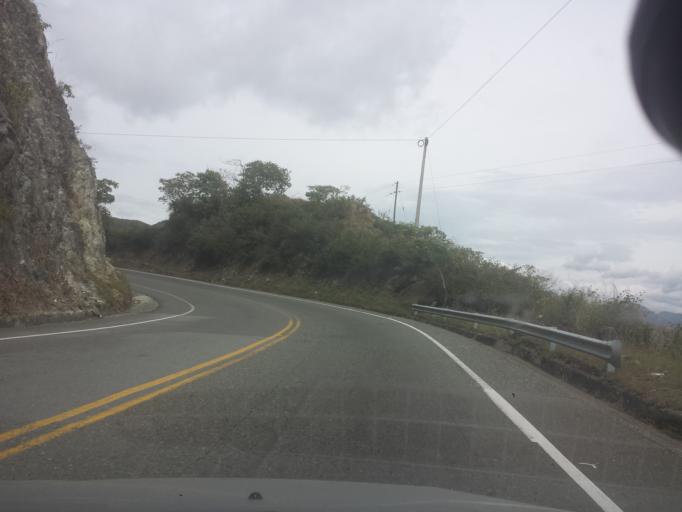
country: CO
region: Antioquia
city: Antioquia
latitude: 6.6121
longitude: -75.8551
